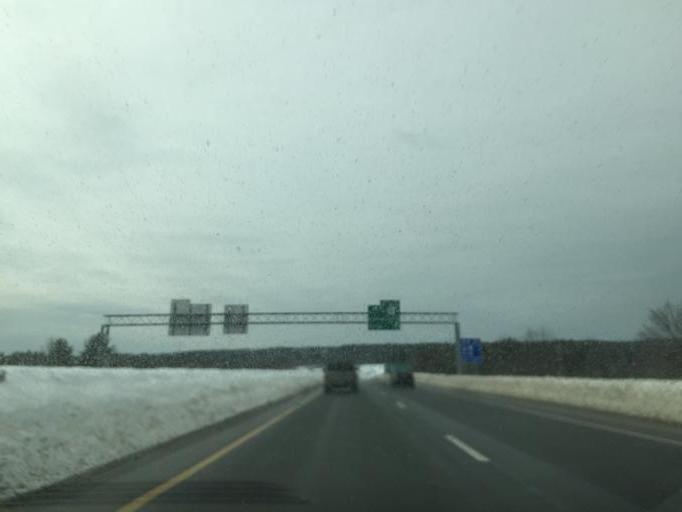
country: US
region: New Hampshire
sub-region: Strafford County
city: Rochester
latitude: 43.3251
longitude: -70.9884
